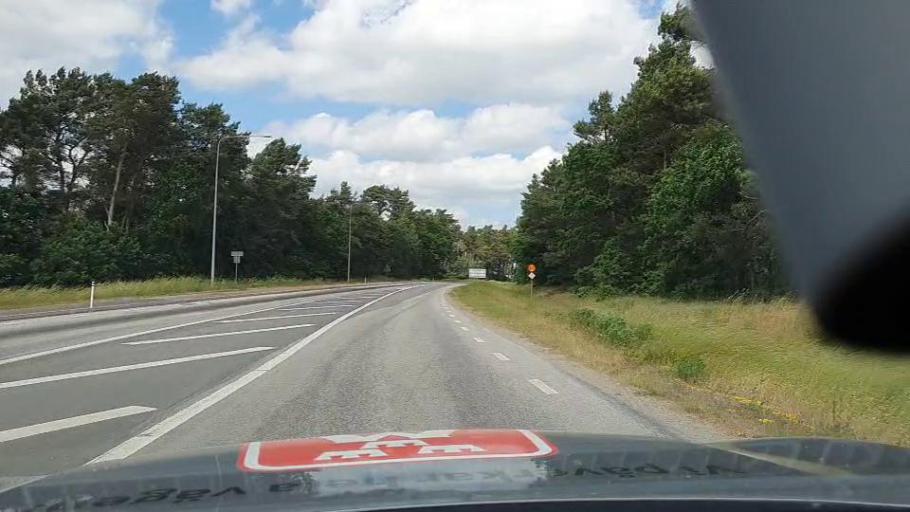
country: SE
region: Blekinge
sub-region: Karlshamns Kommun
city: Morrum
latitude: 56.1120
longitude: 14.6752
